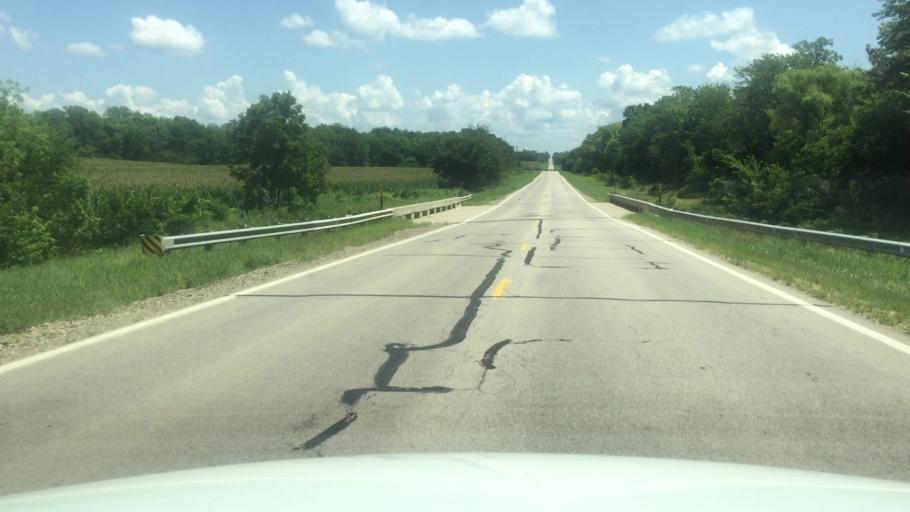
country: US
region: Kansas
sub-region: Brown County
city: Horton
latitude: 39.6674
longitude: -95.5597
